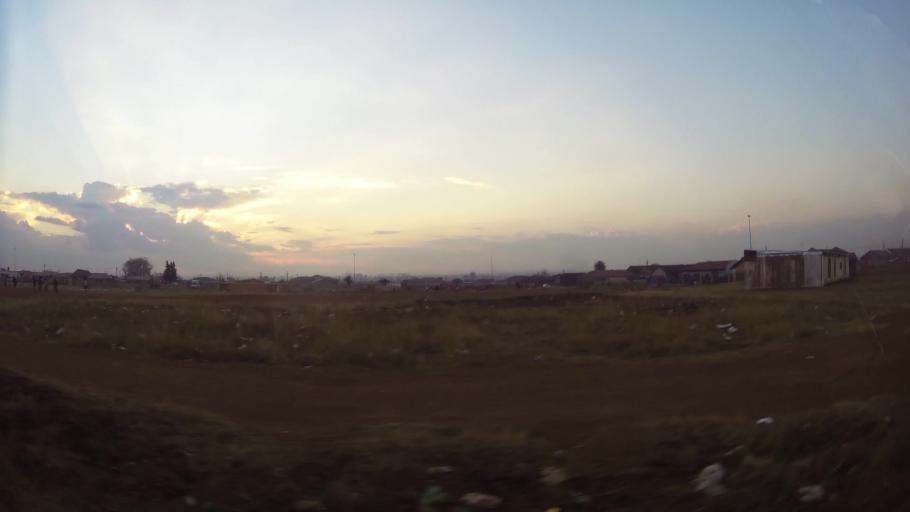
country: ZA
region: Gauteng
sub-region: City of Johannesburg Metropolitan Municipality
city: Orange Farm
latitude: -26.5511
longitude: 27.8830
